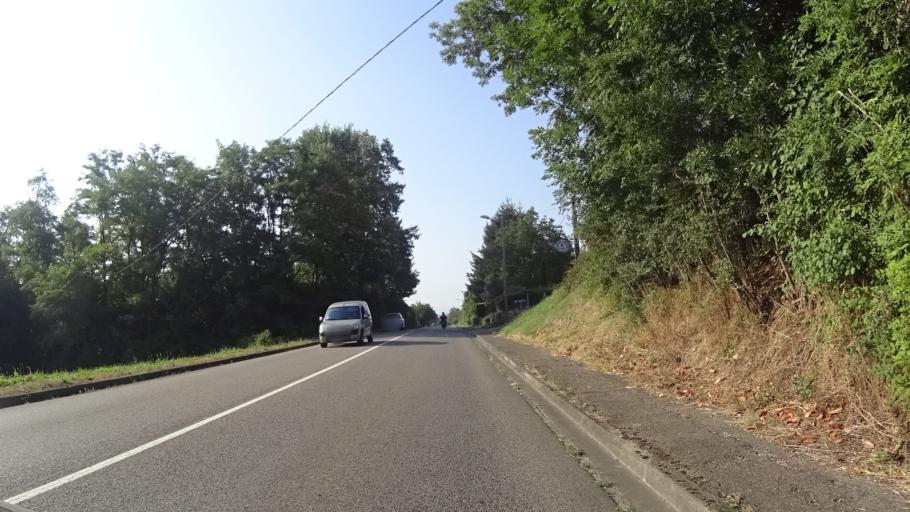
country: FR
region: Midi-Pyrenees
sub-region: Departement de l'Ariege
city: Mirepoix
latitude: 43.0784
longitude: 1.8769
